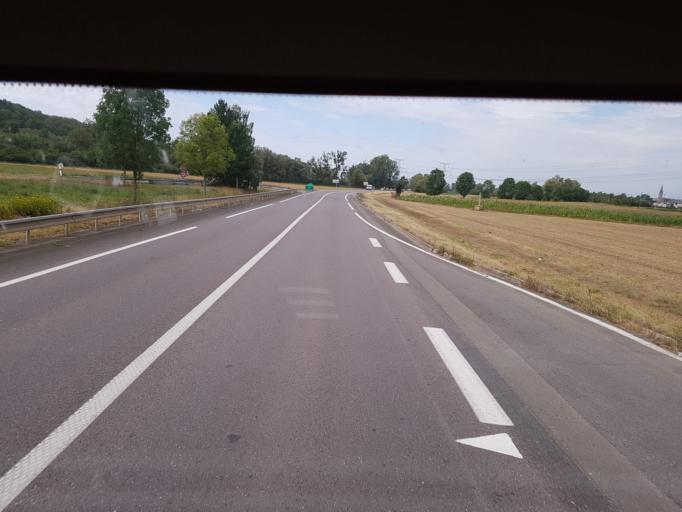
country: FR
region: Lorraine
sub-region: Departement de la Moselle
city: Basse-Ham
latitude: 49.3902
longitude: 6.2599
